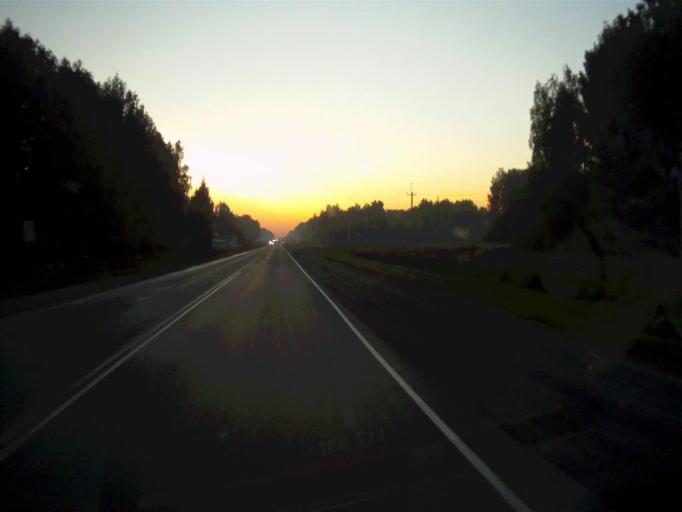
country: RU
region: Chelyabinsk
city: Poletayevo
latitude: 55.2052
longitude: 61.1126
